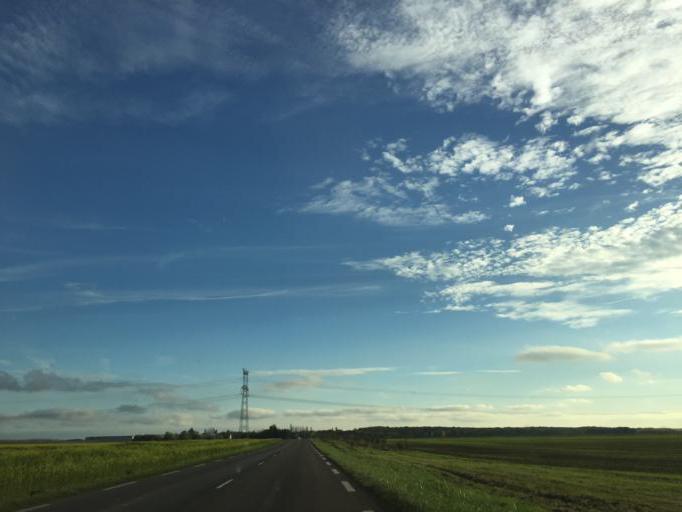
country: FR
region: Ile-de-France
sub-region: Departement de Seine-et-Marne
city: Jouy-le-Chatel
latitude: 48.6088
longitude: 3.1032
